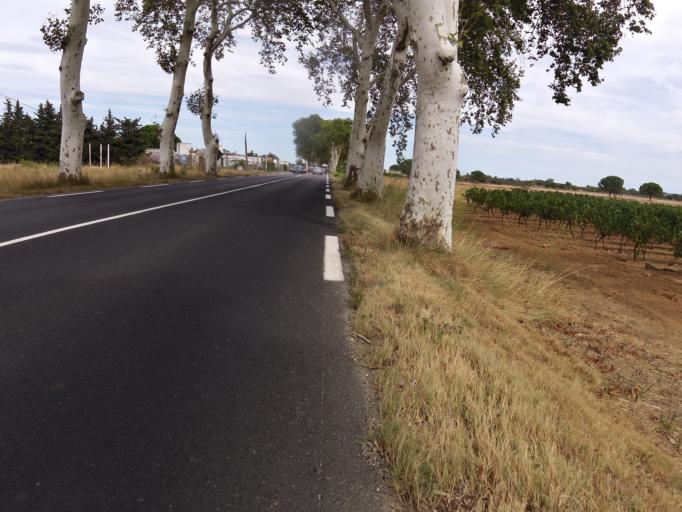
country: FR
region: Languedoc-Roussillon
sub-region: Departement du Gard
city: Codognan
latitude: 43.7192
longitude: 4.2052
